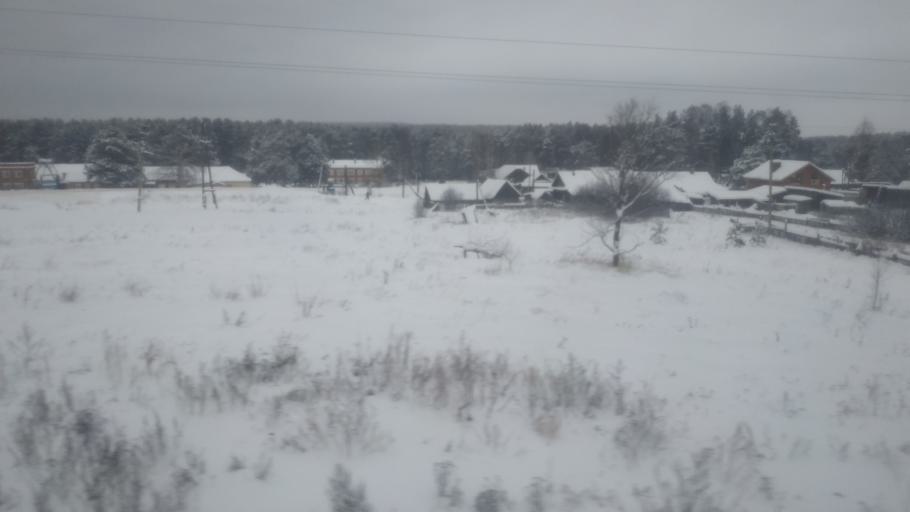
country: RU
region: Udmurtiya
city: Pychas
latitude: 56.5052
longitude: 52.4526
